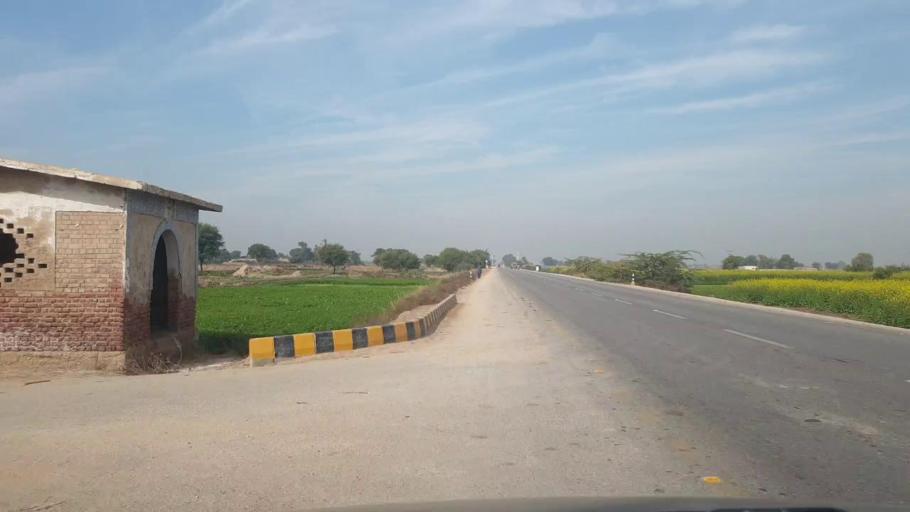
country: PK
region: Sindh
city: Shahpur Chakar
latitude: 26.1821
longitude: 68.5950
